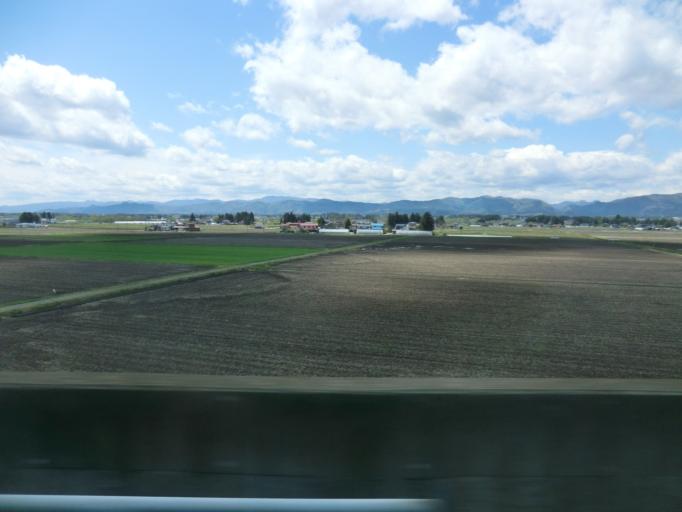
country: JP
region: Iwate
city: Hanamaki
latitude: 39.4736
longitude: 141.1750
